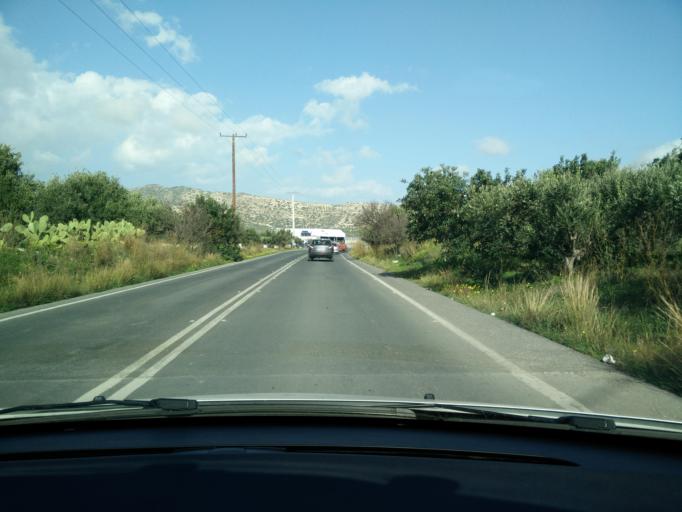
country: GR
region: Crete
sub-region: Nomos Lasithiou
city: Kato Chorio
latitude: 35.0416
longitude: 25.7714
